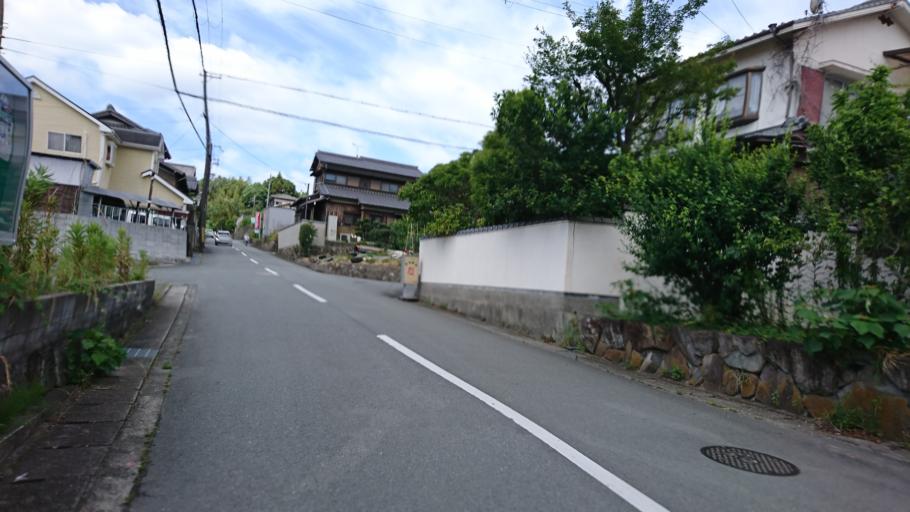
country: JP
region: Hyogo
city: Shirahamacho-usazakiminami
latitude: 34.7966
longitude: 134.7439
